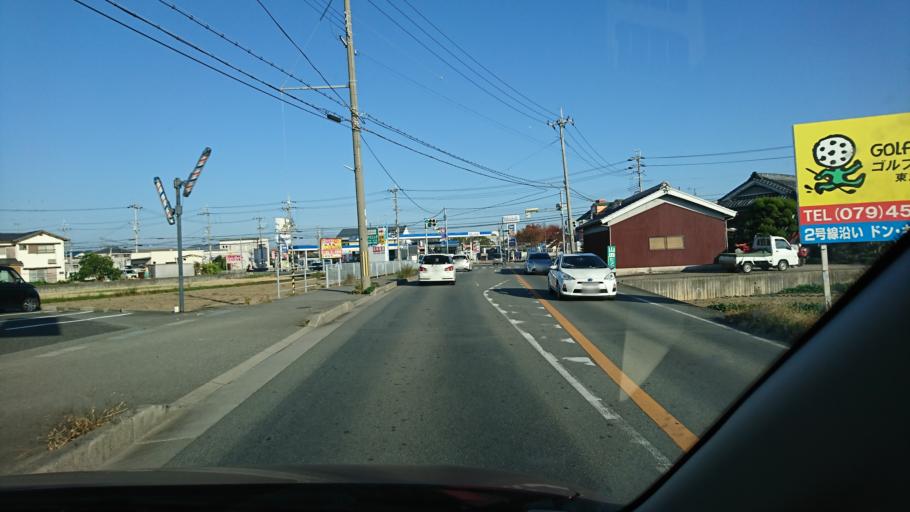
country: JP
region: Hyogo
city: Kakogawacho-honmachi
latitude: 34.7619
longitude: 134.8854
